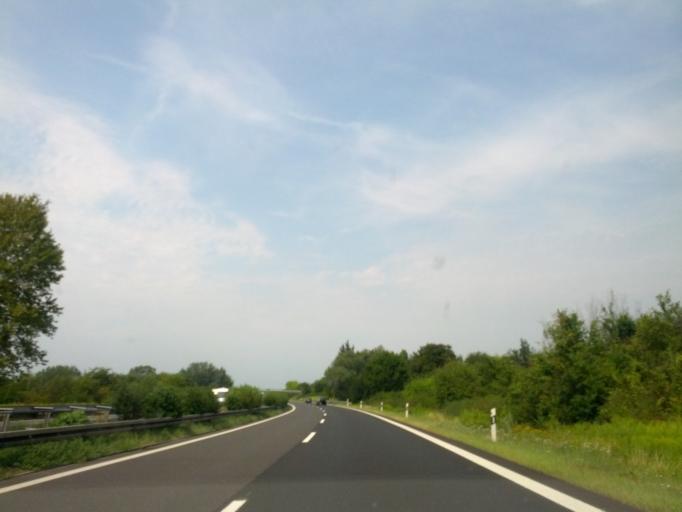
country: DE
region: Brandenburg
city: Wustermark
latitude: 52.4855
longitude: 12.9641
